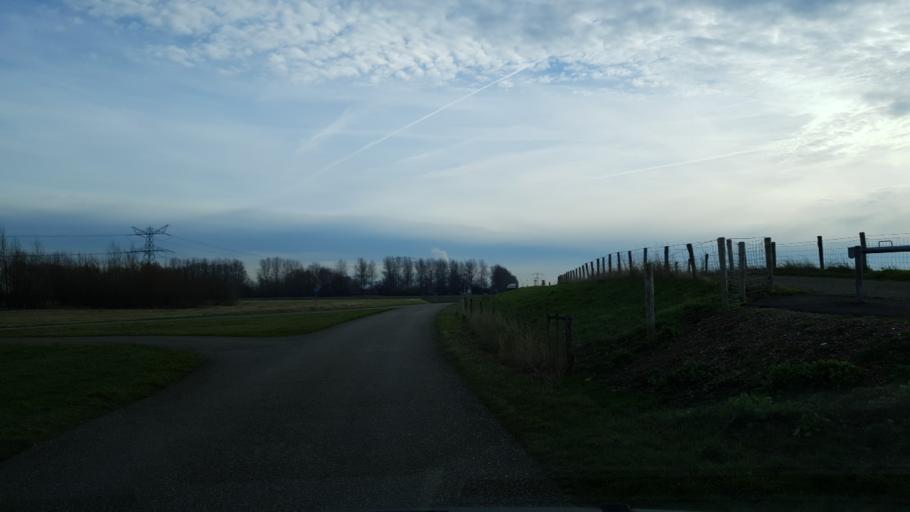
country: NL
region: North Brabant
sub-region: Gemeente Woensdrecht
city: Woensdrecht
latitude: 51.3953
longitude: 4.2322
